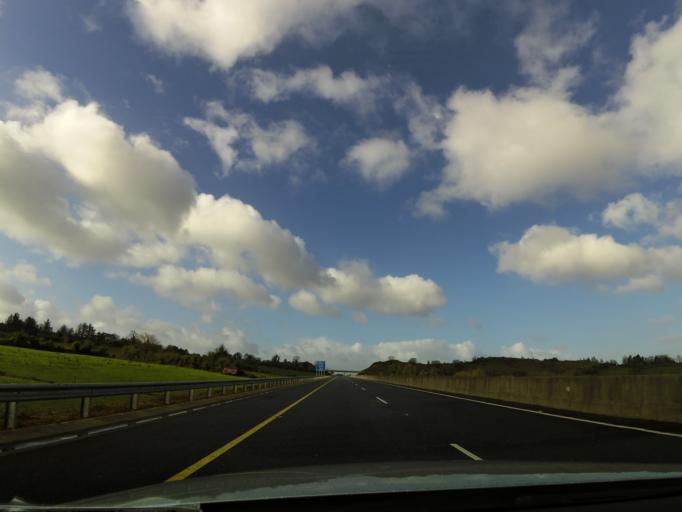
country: IE
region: Munster
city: Ballina
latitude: 52.7752
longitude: -8.3798
